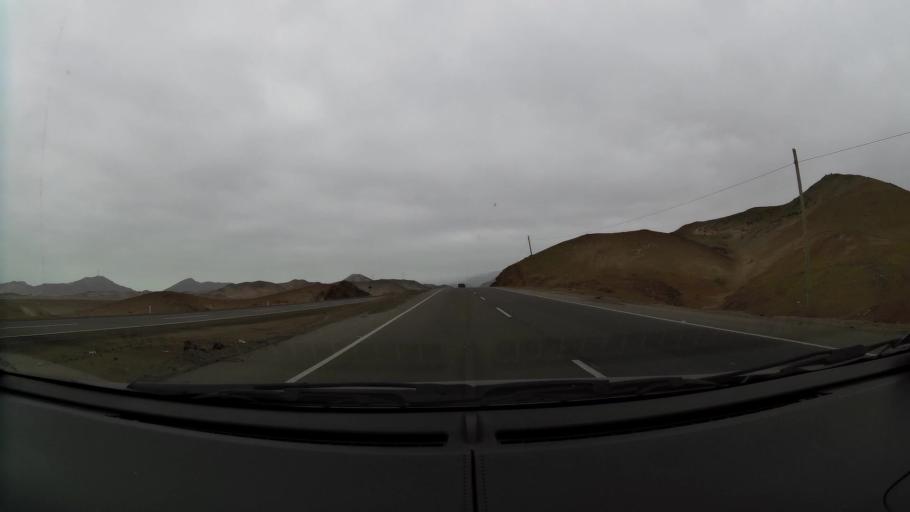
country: PE
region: Lima
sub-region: Barranca
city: Paramonga
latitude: -10.4834
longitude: -77.9146
